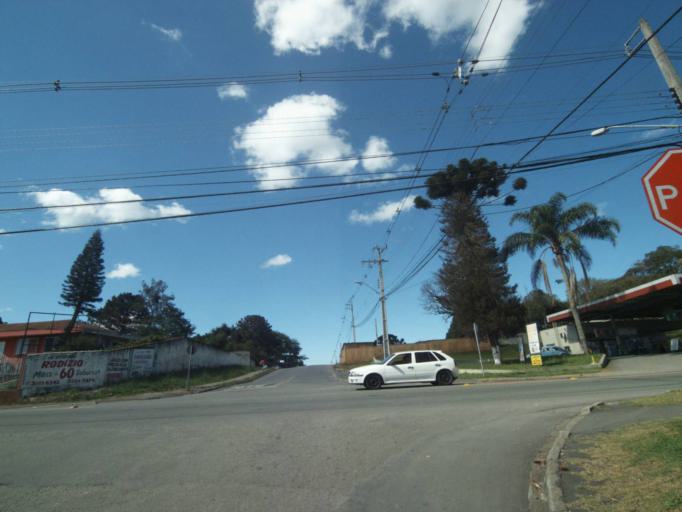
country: BR
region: Parana
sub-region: Curitiba
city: Curitiba
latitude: -25.3778
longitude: -49.2430
